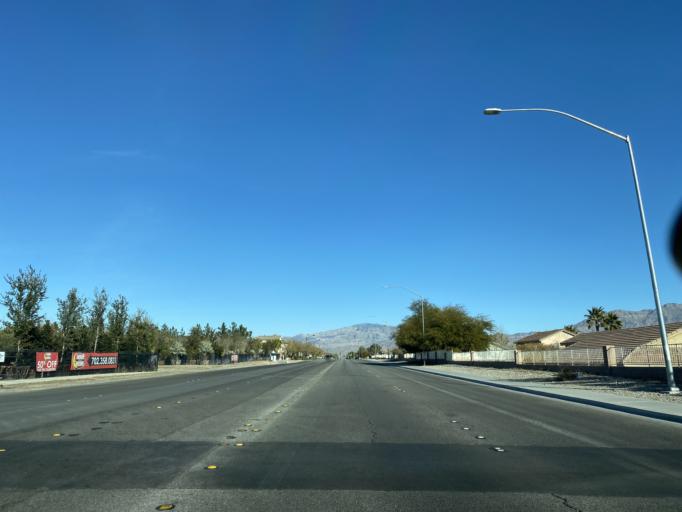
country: US
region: Nevada
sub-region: Clark County
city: Summerlin South
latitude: 36.2937
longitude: -115.2787
